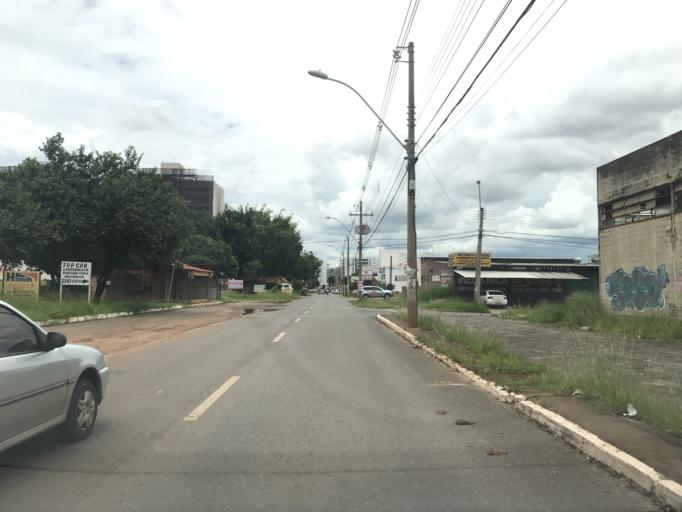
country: BR
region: Federal District
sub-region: Brasilia
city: Brasilia
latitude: -15.8252
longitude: -47.9567
